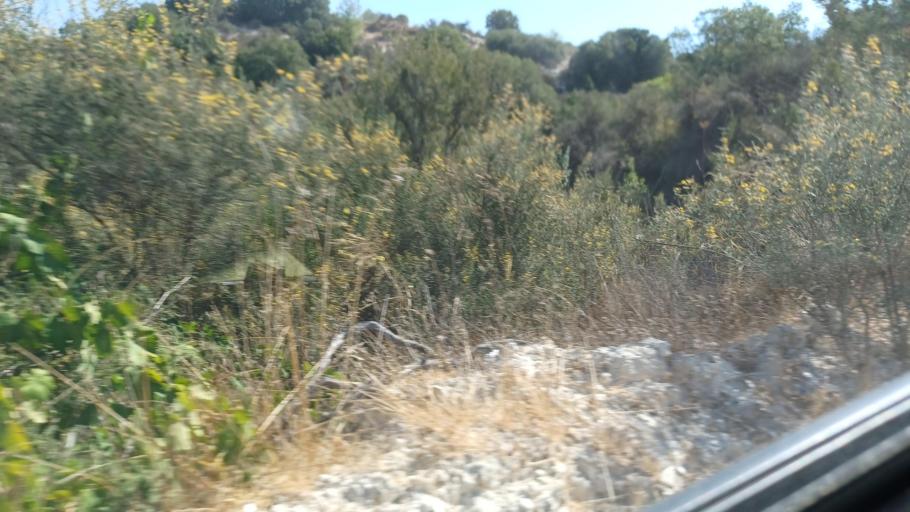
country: CY
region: Pafos
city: Mesogi
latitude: 34.8803
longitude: 32.5320
